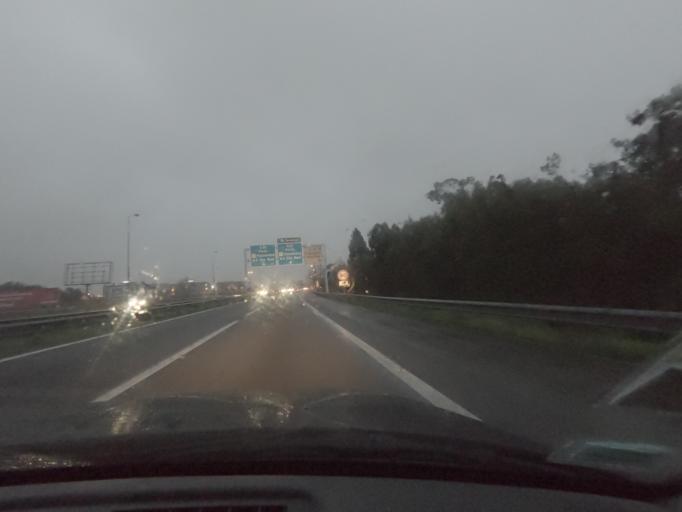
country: PT
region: Porto
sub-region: Matosinhos
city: Santa Cruz do Bispo
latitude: 41.2218
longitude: -8.6923
